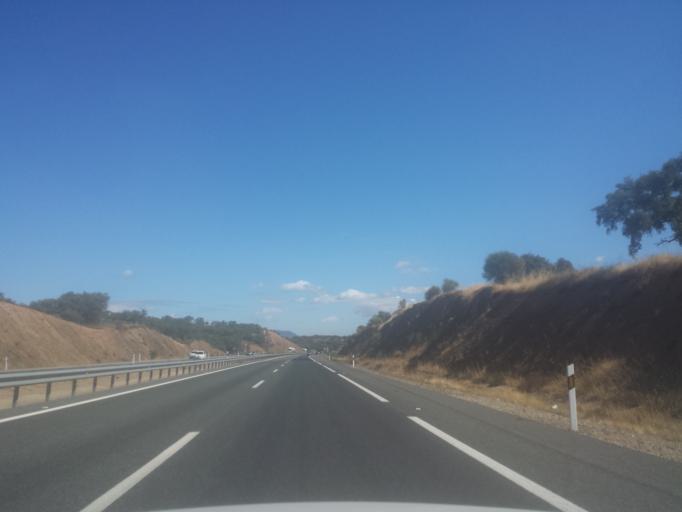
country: ES
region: Andalusia
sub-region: Provincia de Huelva
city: Santa Olalla del Cala
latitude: 37.8719
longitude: -6.2201
